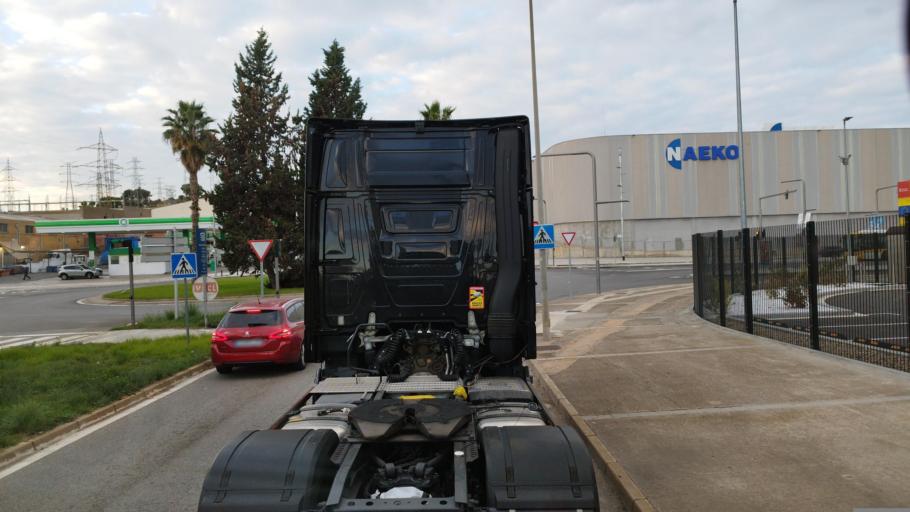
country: ES
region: Catalonia
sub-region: Provincia de Barcelona
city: Sant Boi de Llobregat
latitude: 41.3245
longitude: 2.0329
